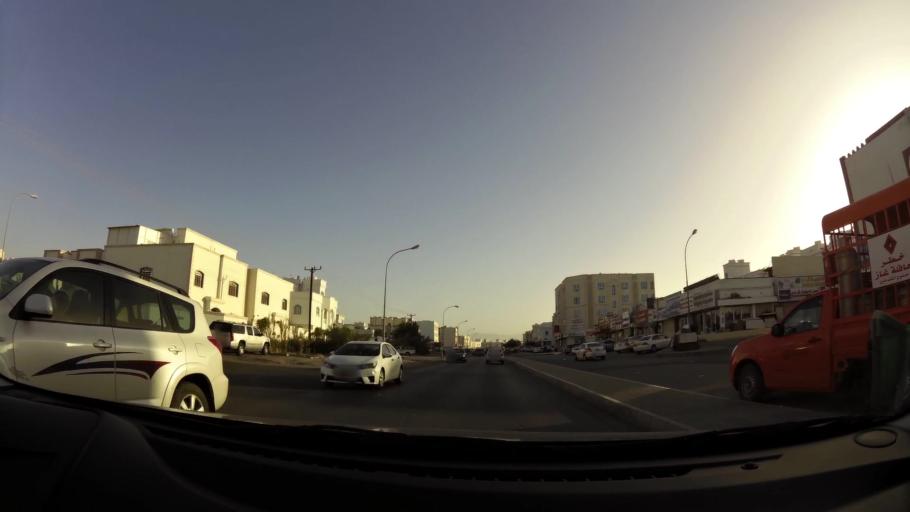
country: OM
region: Muhafazat Masqat
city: As Sib al Jadidah
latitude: 23.6062
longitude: 58.2265
